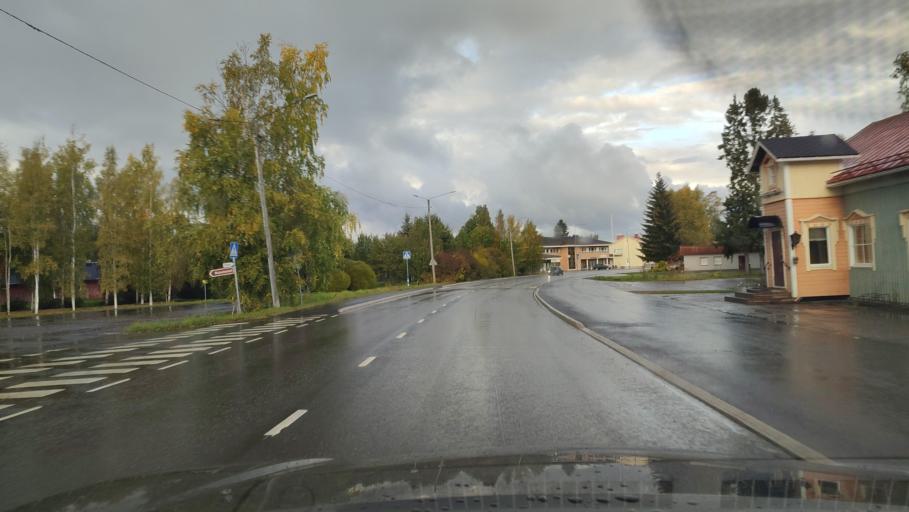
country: FI
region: Southern Ostrobothnia
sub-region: Suupohja
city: Karijoki
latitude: 62.3069
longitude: 21.7028
